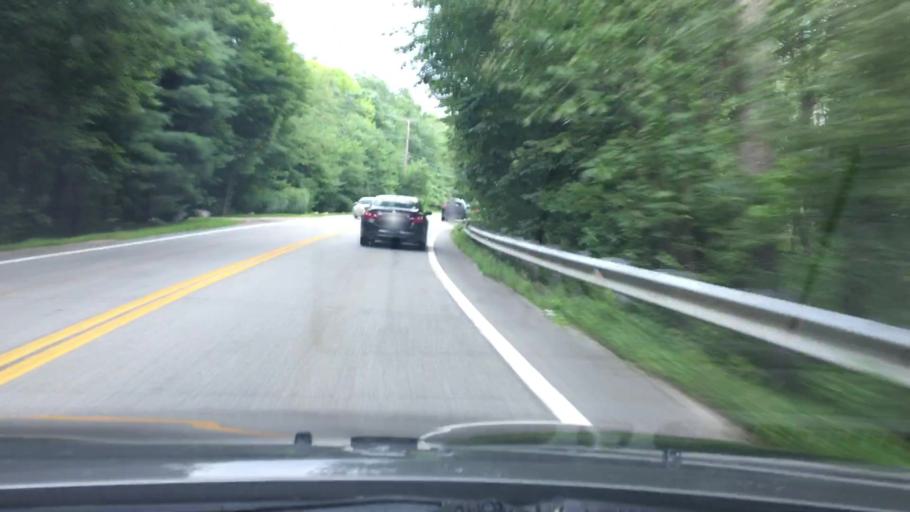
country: US
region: Rhode Island
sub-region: Providence County
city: Cumberland
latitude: 41.9962
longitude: -71.4161
